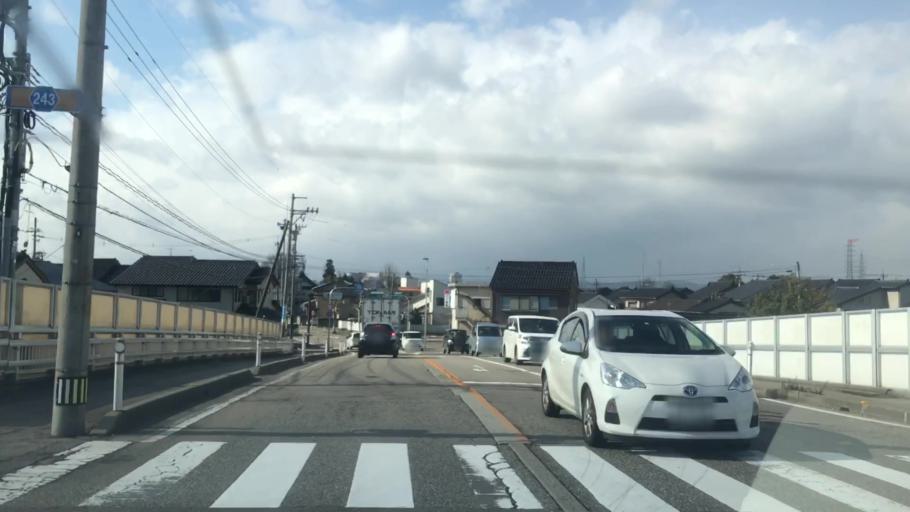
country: JP
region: Toyama
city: Takaoka
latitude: 36.7361
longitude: 137.0405
